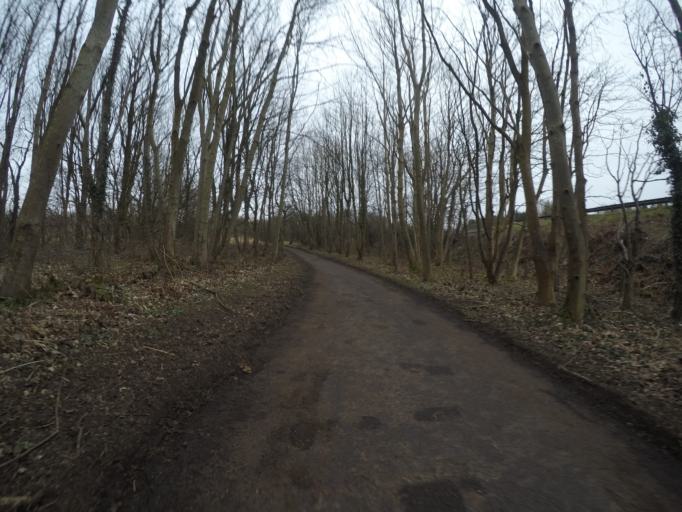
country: GB
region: Scotland
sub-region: North Ayrshire
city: Kilwinning
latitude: 55.6413
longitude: -4.6889
